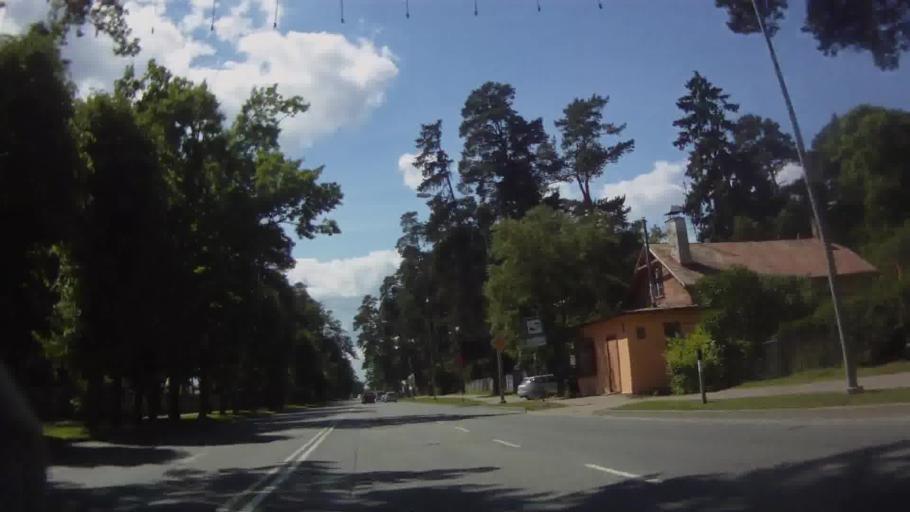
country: LV
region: Jurmala
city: Jurmala
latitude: 56.9726
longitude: 23.8134
